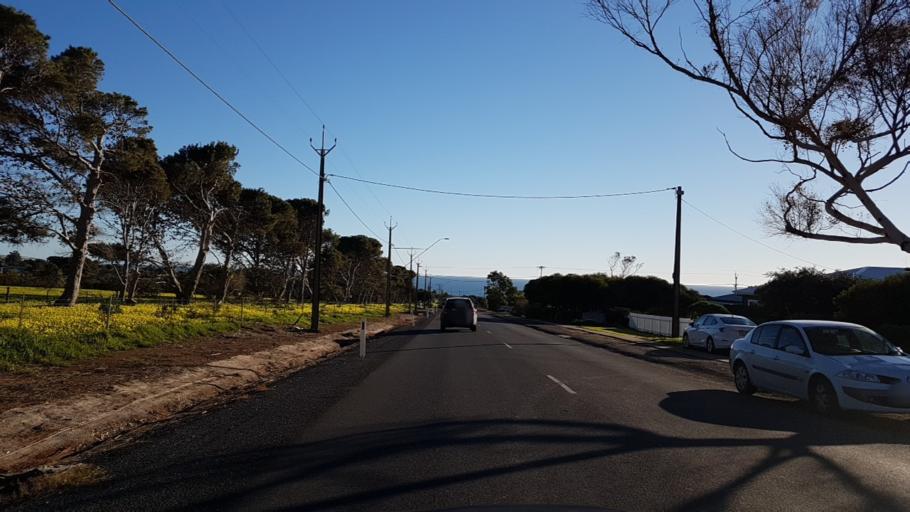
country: AU
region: South Australia
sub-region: Onkaparinga
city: Port Willunga
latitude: -35.3292
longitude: 138.4578
